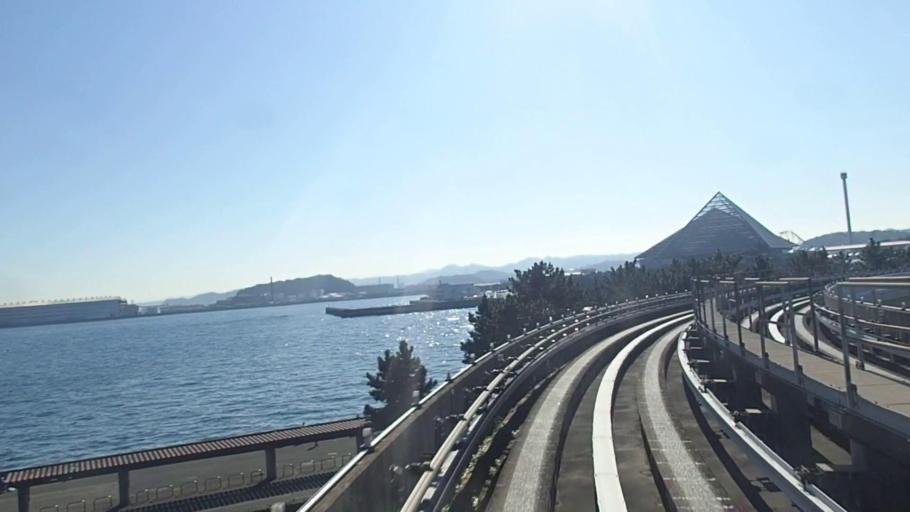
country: JP
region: Kanagawa
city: Yokosuka
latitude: 35.3412
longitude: 139.6502
